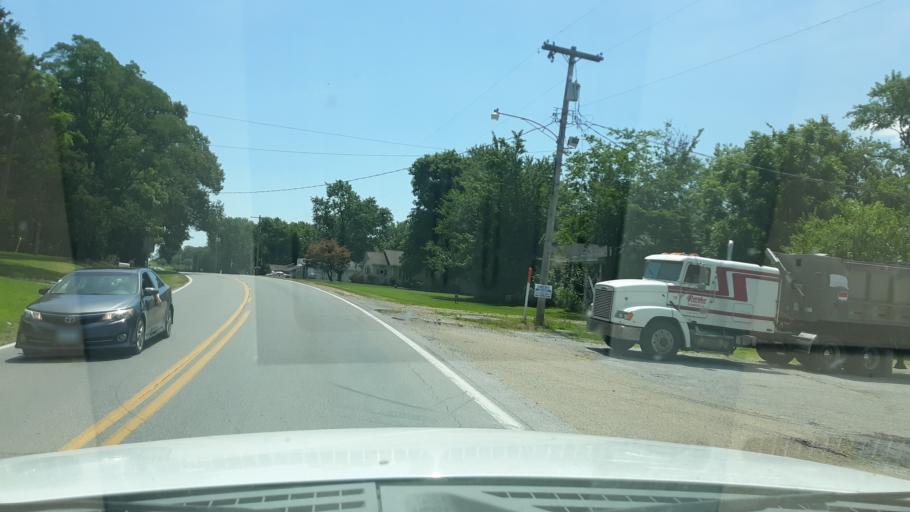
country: US
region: Illinois
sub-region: Saline County
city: Eldorado
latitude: 37.8050
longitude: -88.4380
